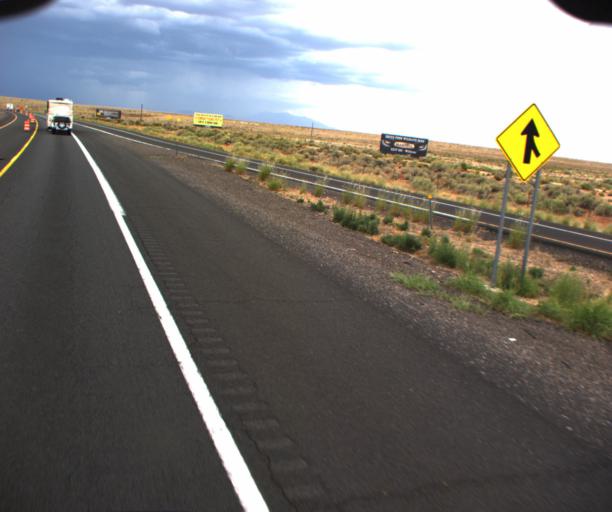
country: US
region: Arizona
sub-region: Coconino County
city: LeChee
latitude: 35.1180
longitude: -111.0932
